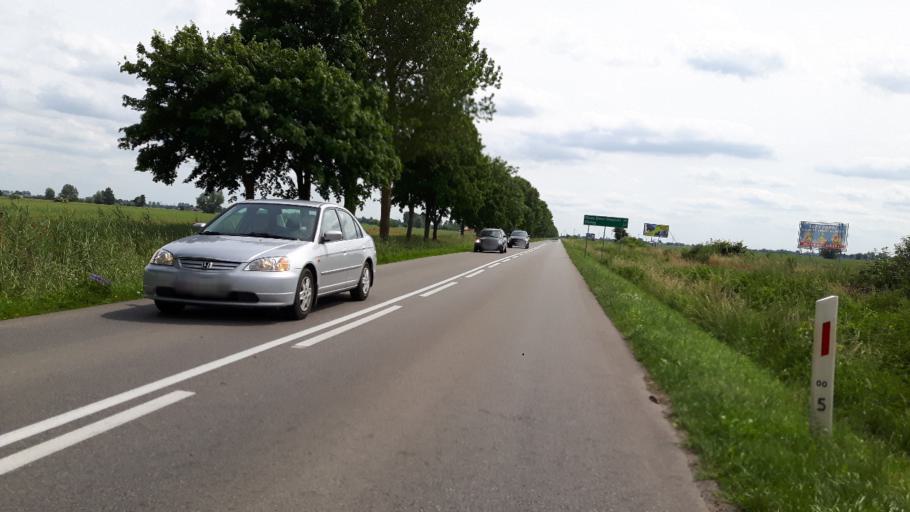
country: PL
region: Pomeranian Voivodeship
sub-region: Powiat nowodworski
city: Stegna
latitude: 54.3223
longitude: 19.1104
